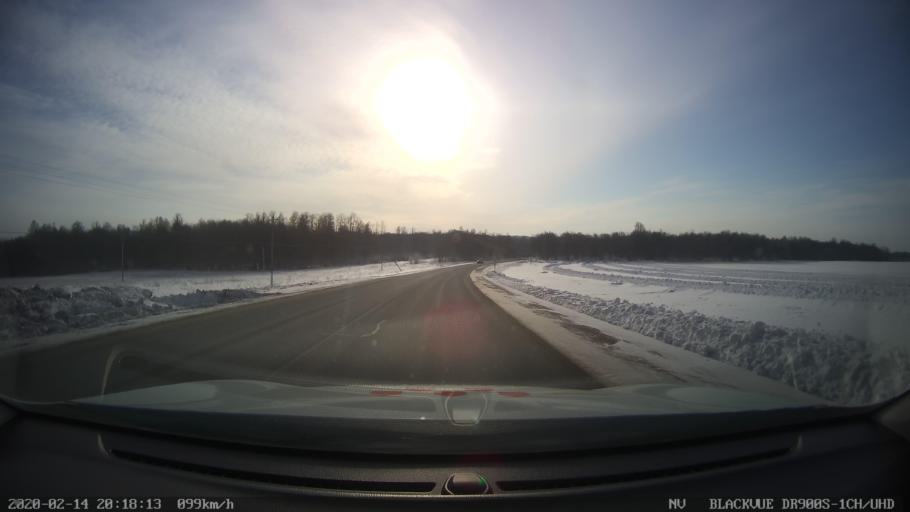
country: RU
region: Tatarstan
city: Verkhniy Uslon
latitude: 55.5892
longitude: 48.8859
